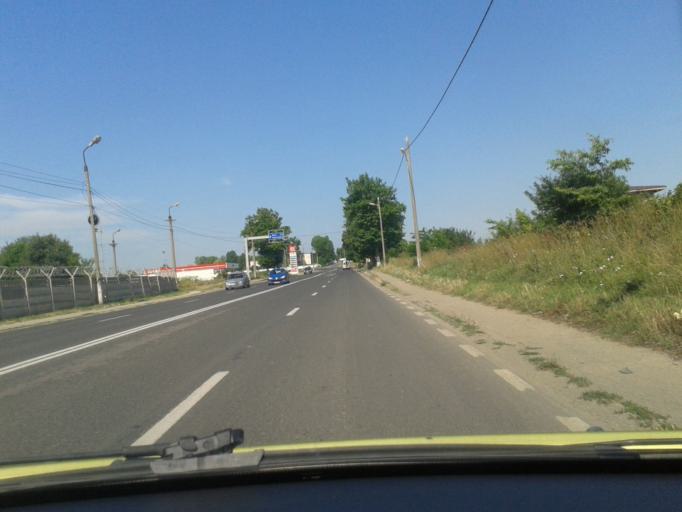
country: RO
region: Constanta
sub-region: Municipiul Mangalia
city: Mangalia
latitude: 43.8079
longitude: 28.5670
